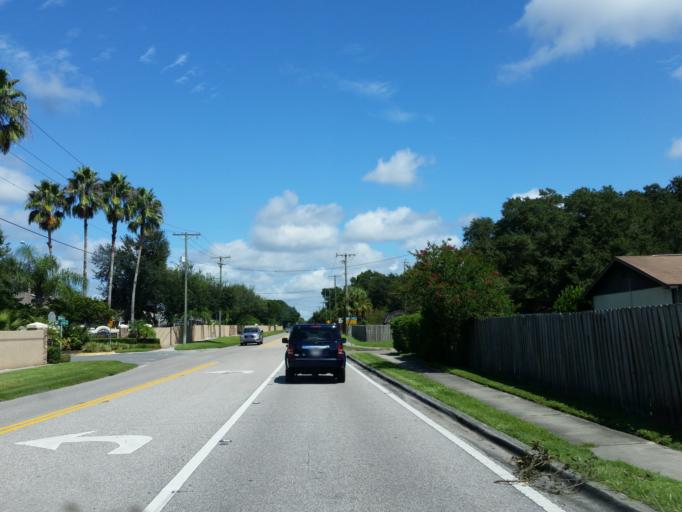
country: US
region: Florida
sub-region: Hillsborough County
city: Brandon
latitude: 27.9147
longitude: -82.2856
